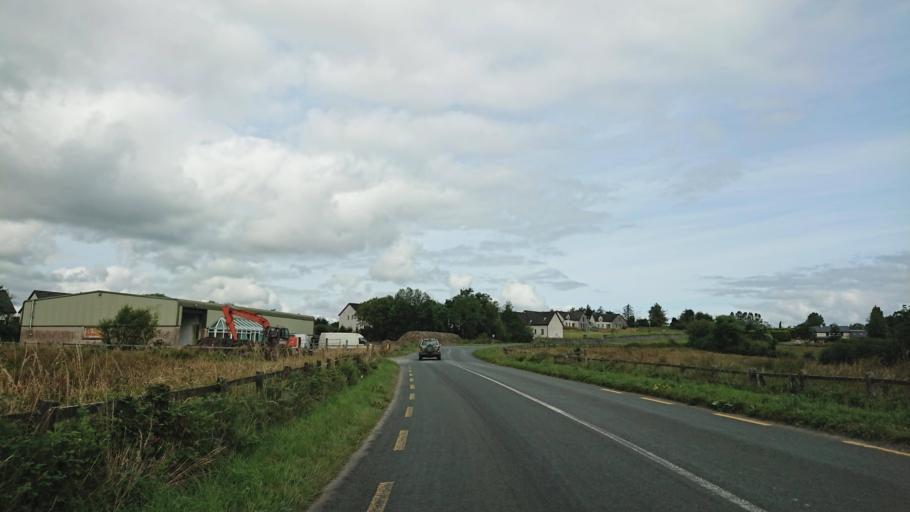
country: IE
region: Connaught
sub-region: County Leitrim
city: Carrick-on-Shannon
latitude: 54.0523
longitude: -8.0389
